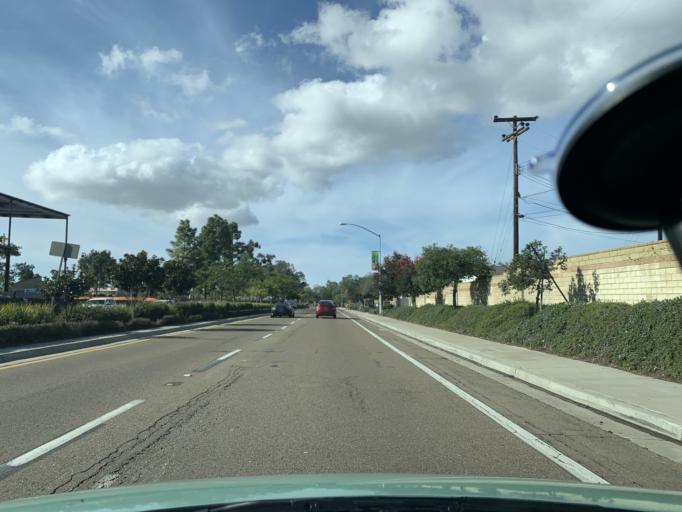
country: US
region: California
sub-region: San Diego County
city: San Diego
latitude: 32.7922
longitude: -117.1669
